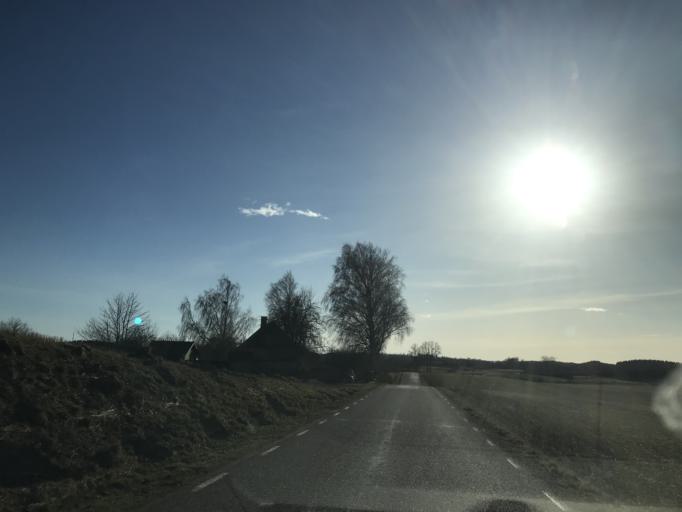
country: SE
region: Skane
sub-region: Ystads Kommun
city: Ystad
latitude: 55.5365
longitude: 13.7865
